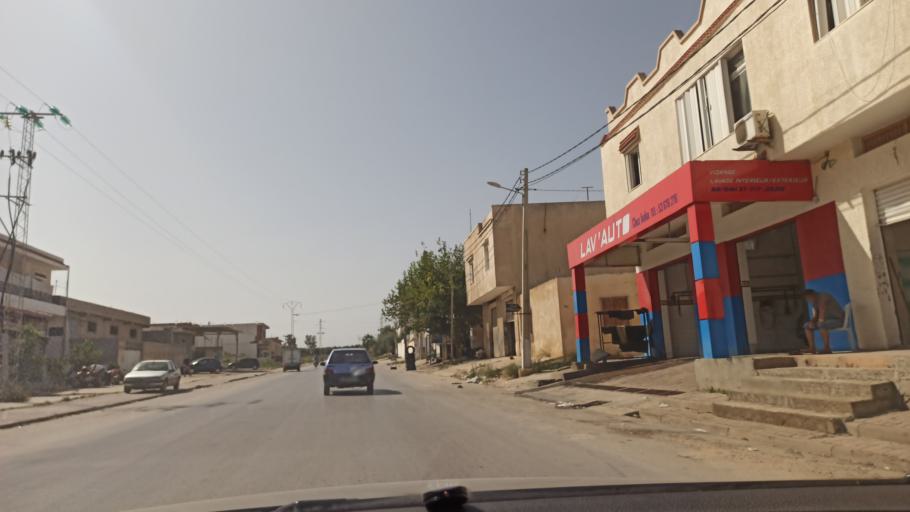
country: TN
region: Manouba
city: Manouba
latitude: 36.7532
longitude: 10.1012
